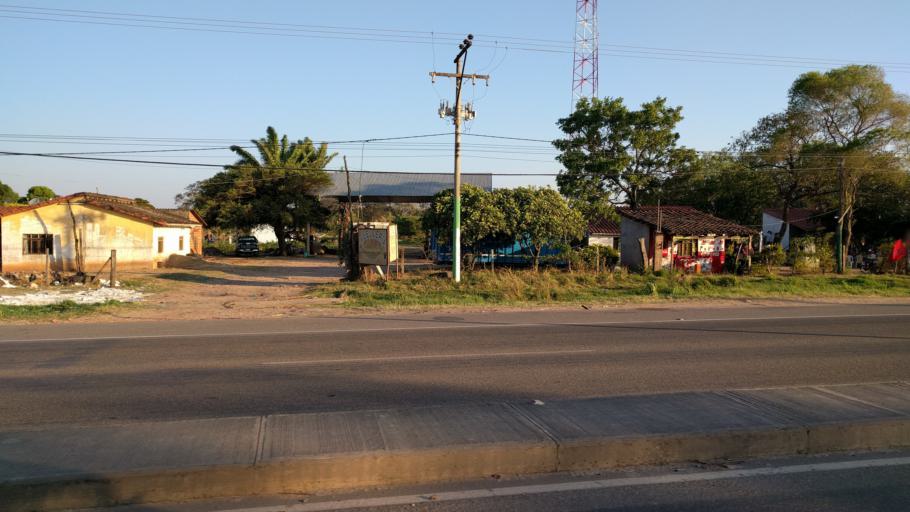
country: BO
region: Santa Cruz
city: Cotoca
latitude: -17.7613
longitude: -63.0223
